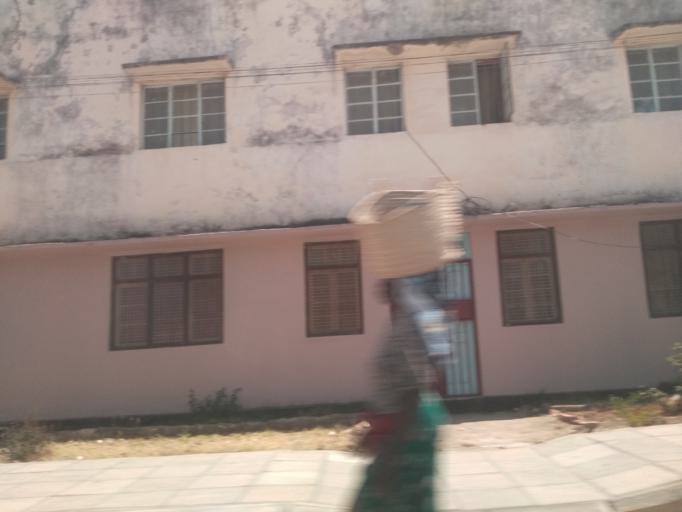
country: TZ
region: Dodoma
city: Dodoma
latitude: -6.1759
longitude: 35.7480
